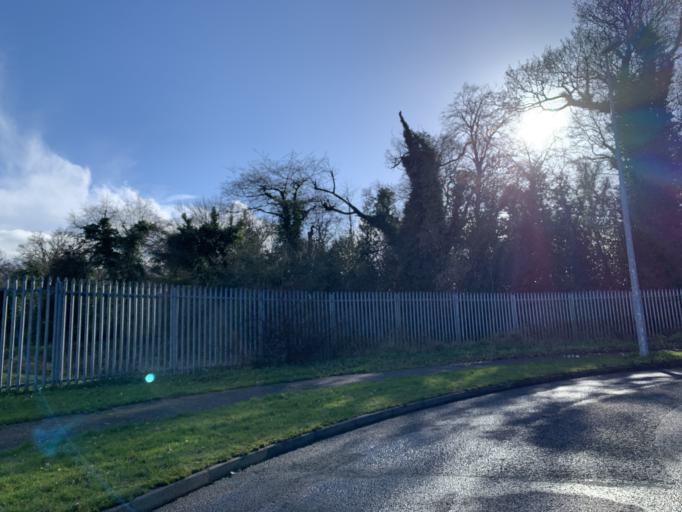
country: IE
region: Leinster
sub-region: Kildare
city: Celbridge
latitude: 53.3323
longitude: -6.5602
